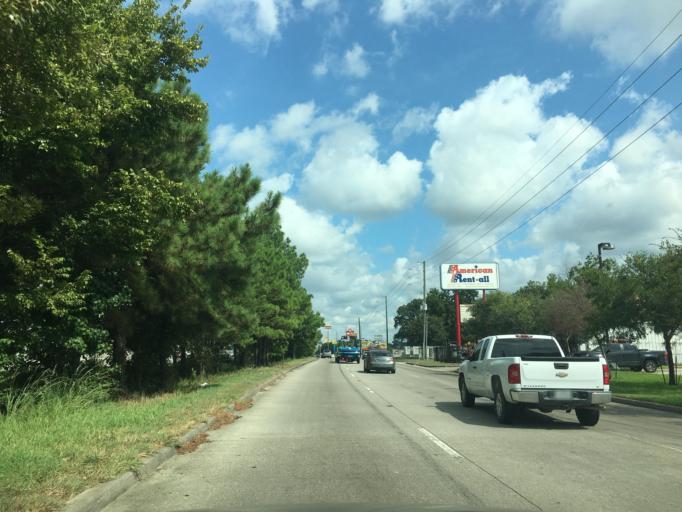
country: US
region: Texas
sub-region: Harris County
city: Spring
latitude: 30.0684
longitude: -95.4344
